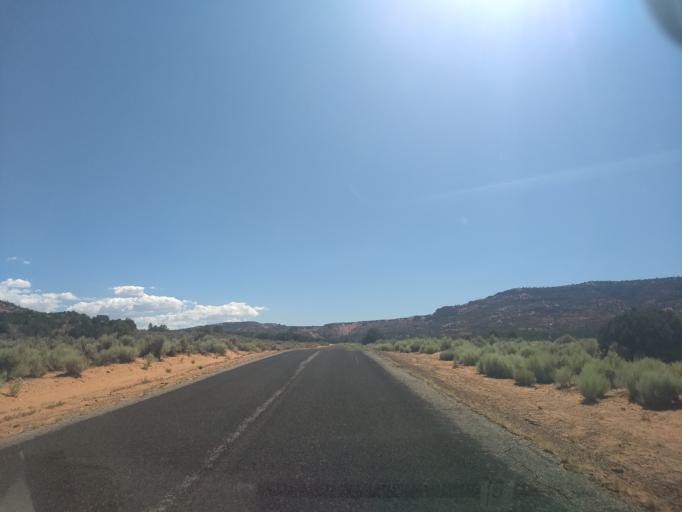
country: US
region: Utah
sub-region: Washington County
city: Hildale
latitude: 37.0158
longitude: -112.8395
